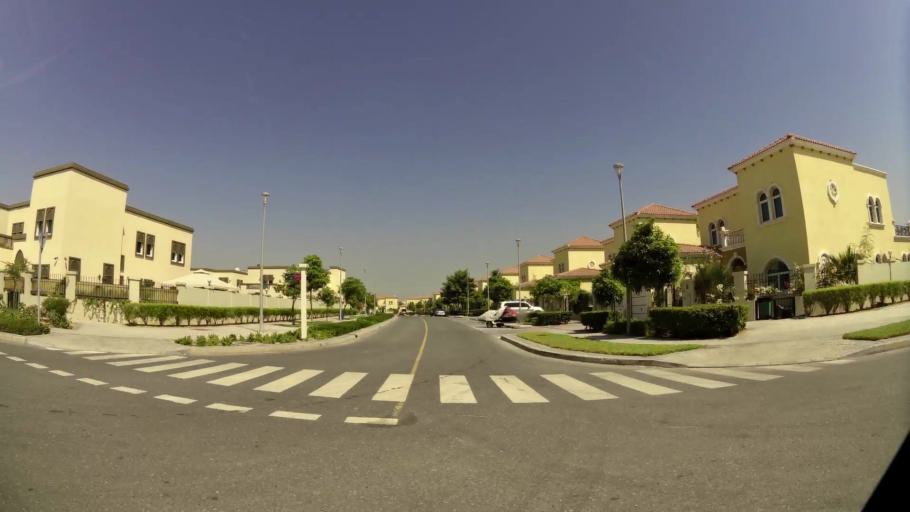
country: AE
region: Dubai
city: Dubai
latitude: 25.0502
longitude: 55.1498
